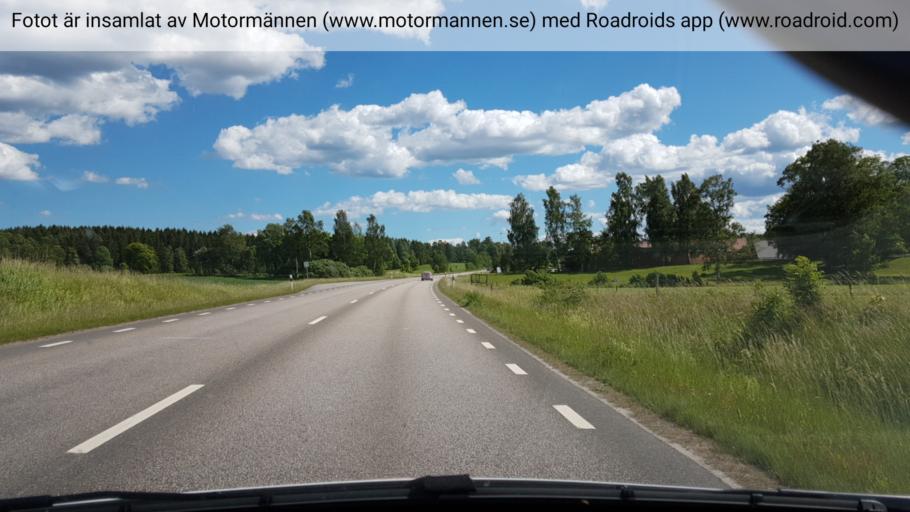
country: SE
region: Vaestra Goetaland
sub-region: Hjo Kommun
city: Hjo
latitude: 58.3334
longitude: 14.2515
